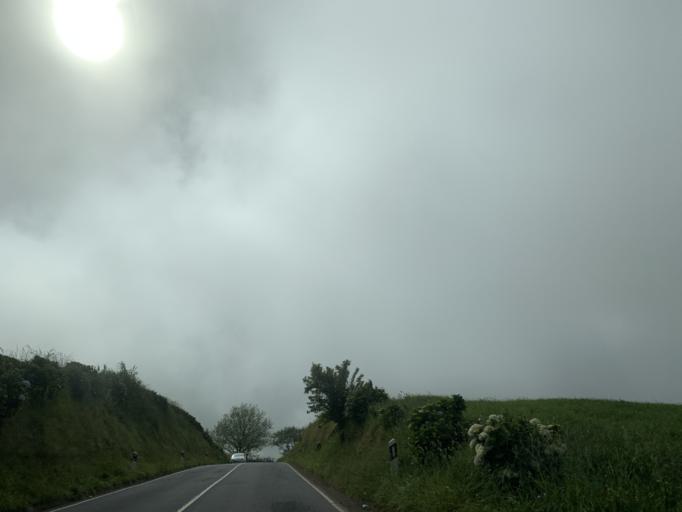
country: PT
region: Azores
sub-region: Ponta Delgada
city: Arrifes
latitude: 37.7733
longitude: -25.7430
